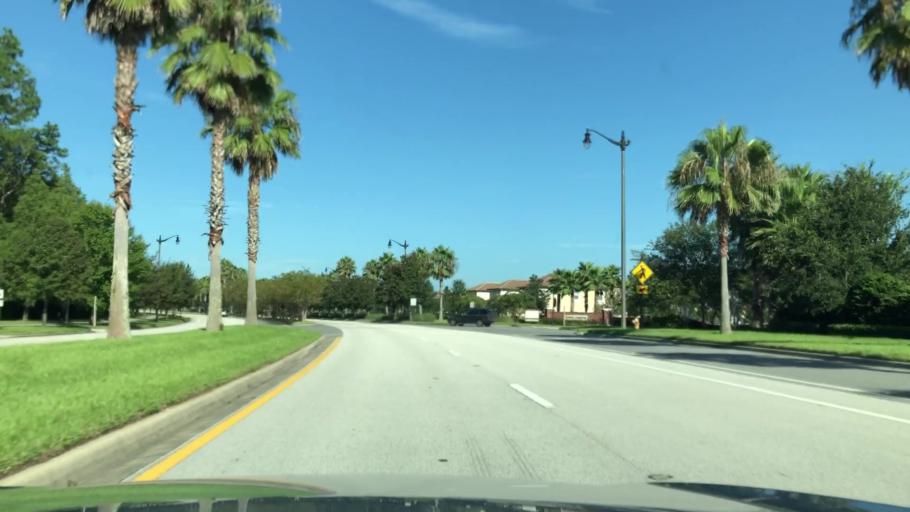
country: US
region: Florida
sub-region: Saint Johns County
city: Palm Valley
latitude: 30.1050
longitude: -81.4208
